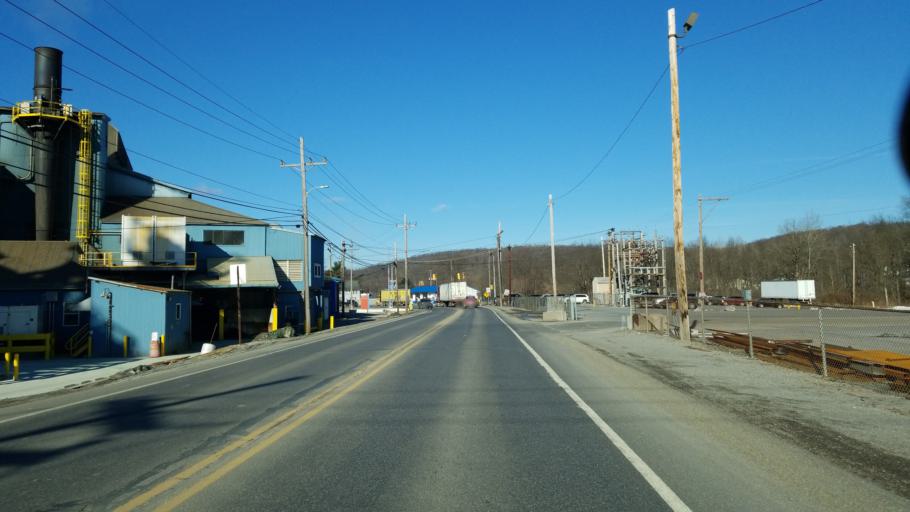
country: US
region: Pennsylvania
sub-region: Jefferson County
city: Brockway
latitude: 41.2412
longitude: -78.7850
